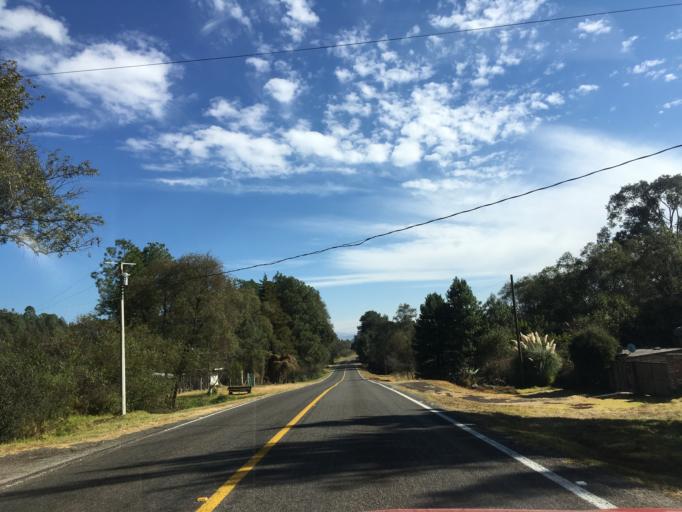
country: MX
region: Michoacan
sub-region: Hidalgo
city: Tierras Coloradas (San Pedro)
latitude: 19.6668
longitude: -100.7131
